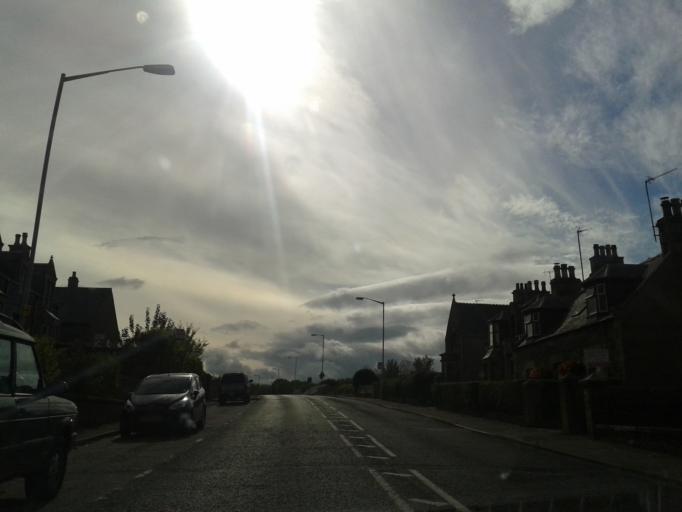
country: GB
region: Scotland
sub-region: Aberdeenshire
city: Portsoy
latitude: 57.6781
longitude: -2.6879
